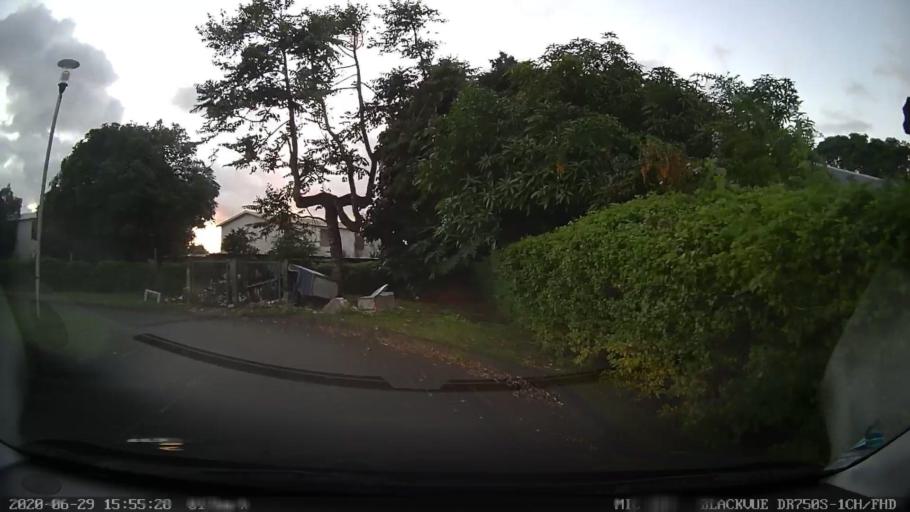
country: RE
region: Reunion
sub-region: Reunion
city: Bras-Panon
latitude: -21.0007
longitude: 55.6952
